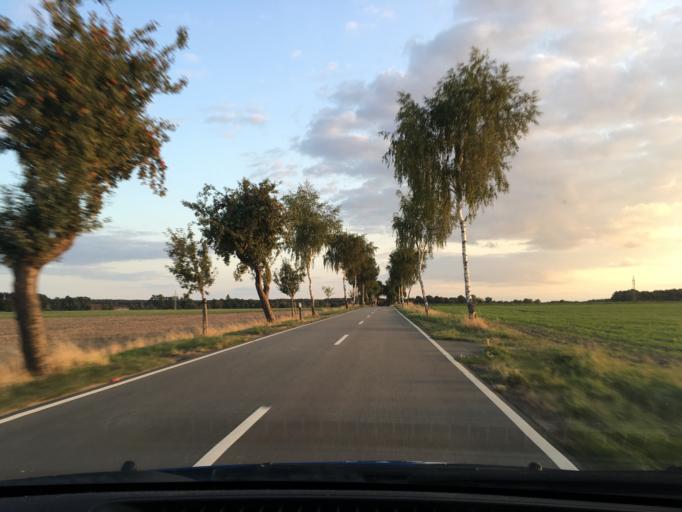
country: DE
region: Lower Saxony
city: Nahrendorf
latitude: 53.1684
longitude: 10.8113
